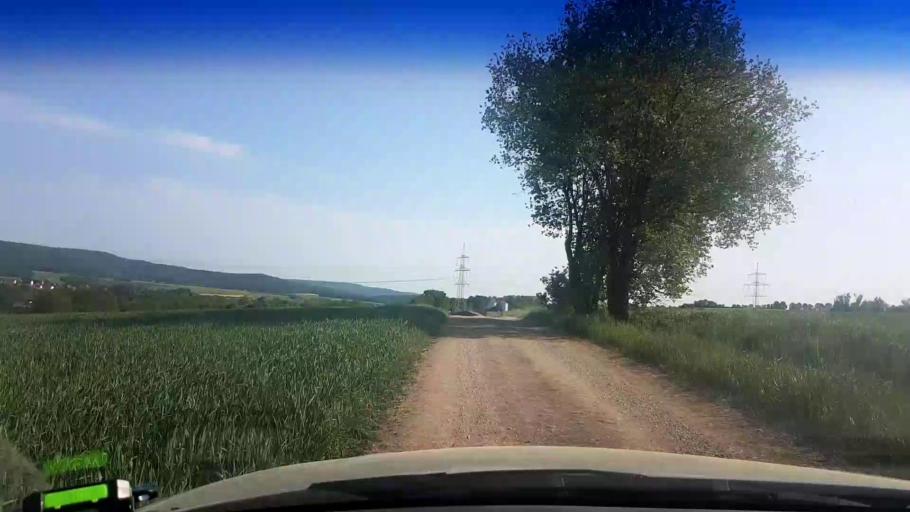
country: DE
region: Bavaria
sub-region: Upper Franconia
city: Memmelsdorf
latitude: 49.9677
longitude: 10.9845
